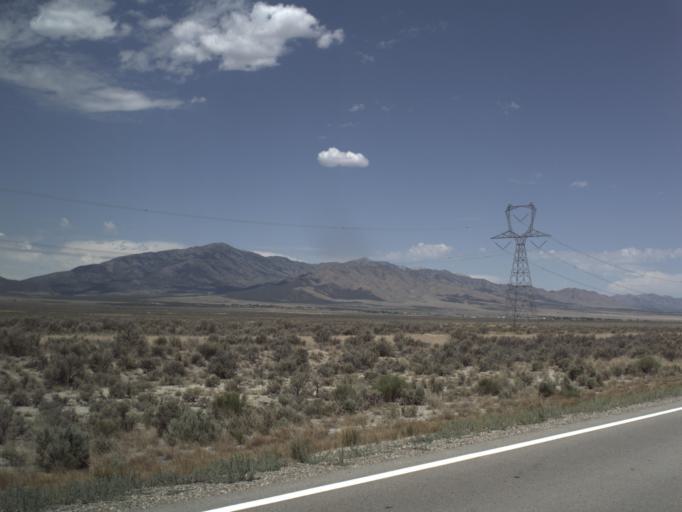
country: US
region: Utah
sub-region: Tooele County
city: Tooele
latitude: 40.2847
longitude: -112.3995
